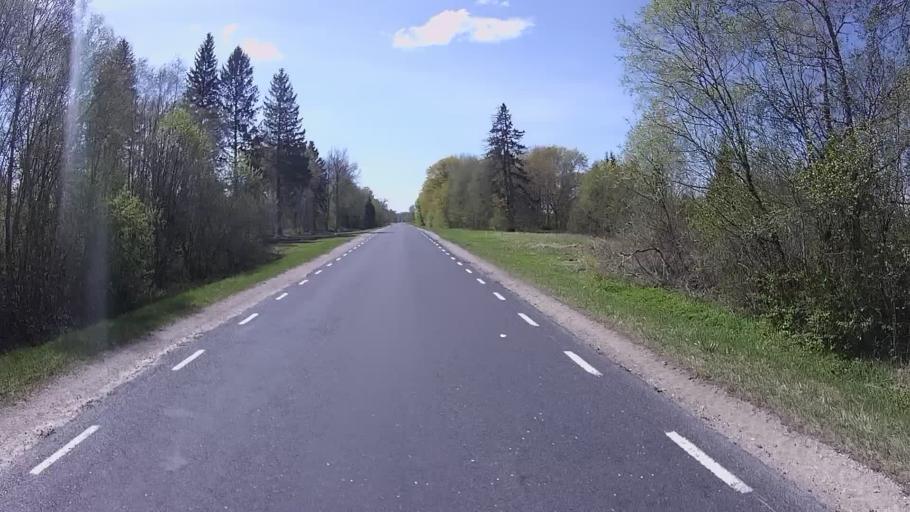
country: EE
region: Laeaene
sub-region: Ridala Parish
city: Uuemoisa
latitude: 59.0186
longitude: 23.7967
